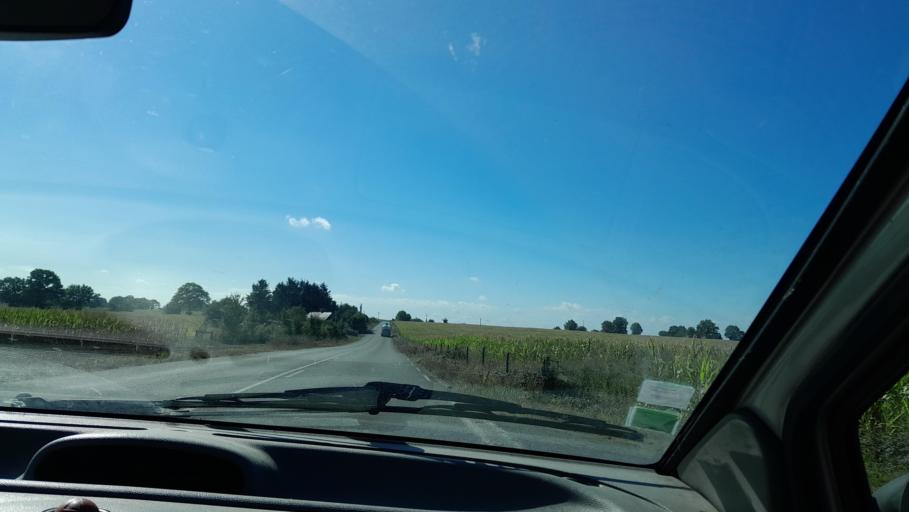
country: FR
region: Pays de la Loire
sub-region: Departement de la Mayenne
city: Ballots
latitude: 47.9145
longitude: -1.0623
